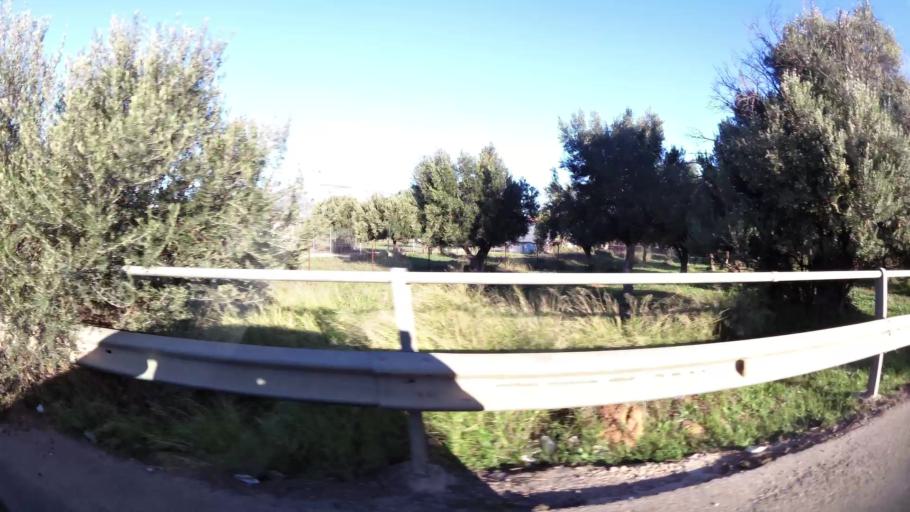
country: GR
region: Attica
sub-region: Nomarchia Anatolikis Attikis
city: Koropi
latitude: 37.9089
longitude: 23.8880
